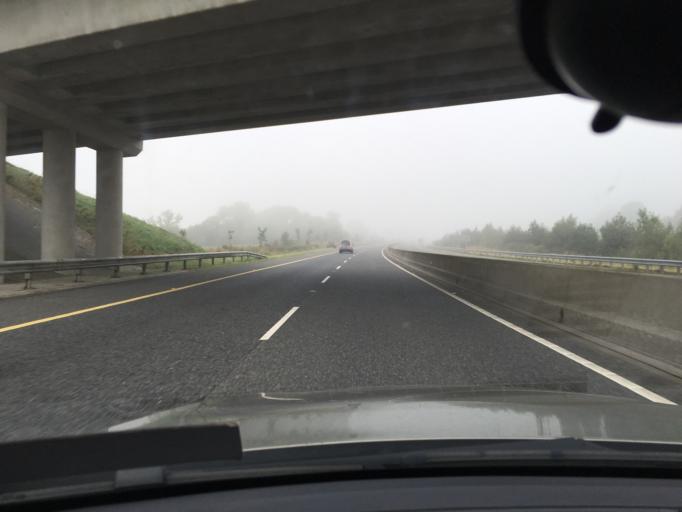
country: IE
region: Leinster
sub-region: An Iarmhi
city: Kilbeggan
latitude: 53.3622
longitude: -7.5205
